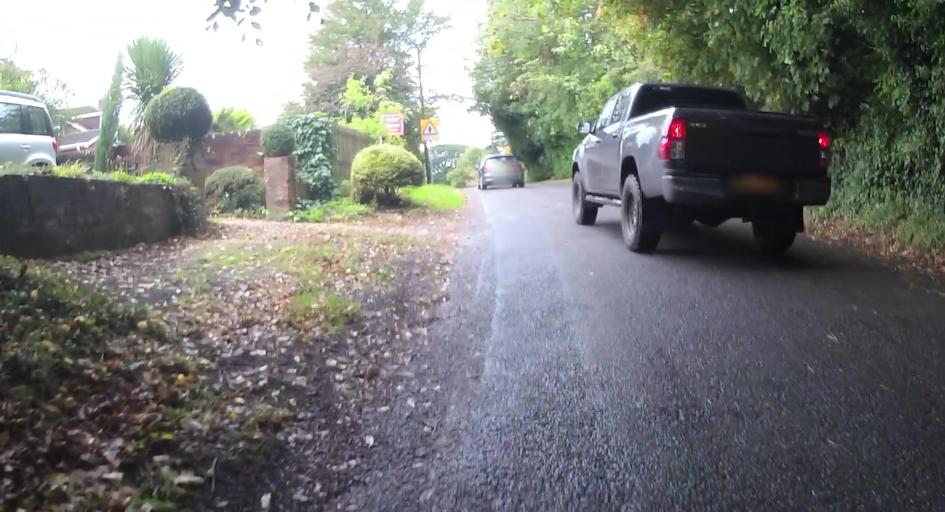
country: GB
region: England
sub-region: Hampshire
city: Tadley
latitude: 51.3119
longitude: -1.1545
